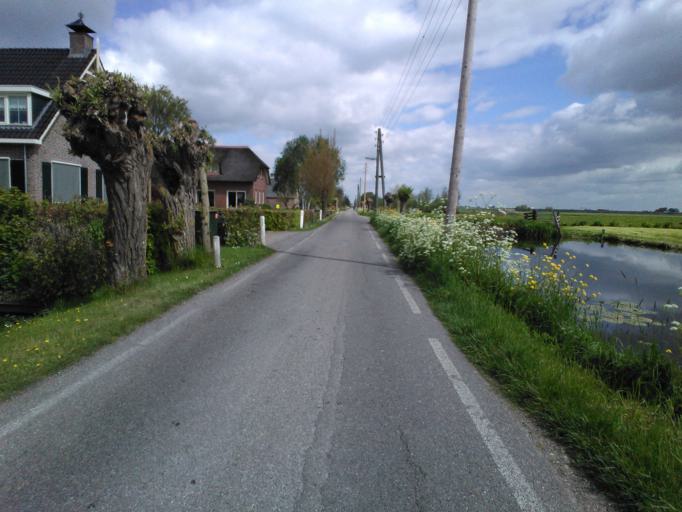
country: NL
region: South Holland
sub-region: Bodegraven-Reeuwijk
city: Bodegraven
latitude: 52.0527
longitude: 4.7943
